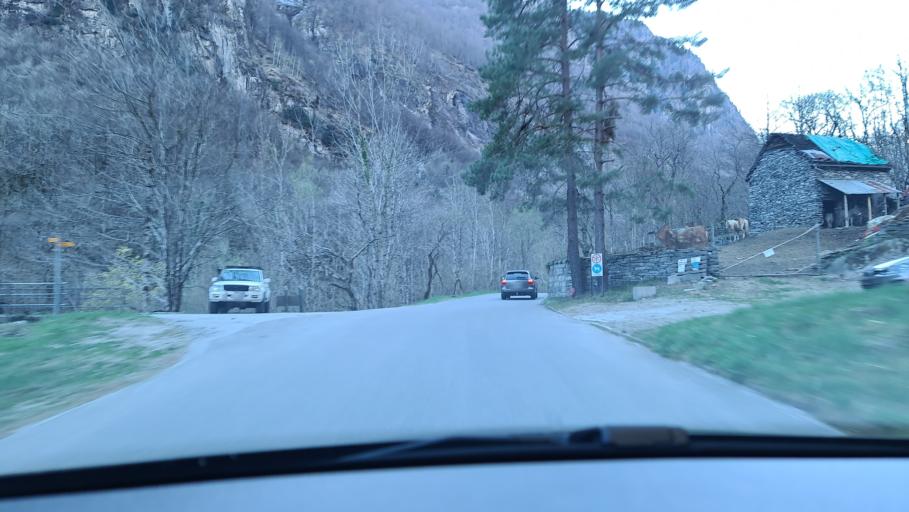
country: CH
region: Ticino
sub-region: Vallemaggia District
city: Cevio
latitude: 46.3537
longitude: 8.5890
